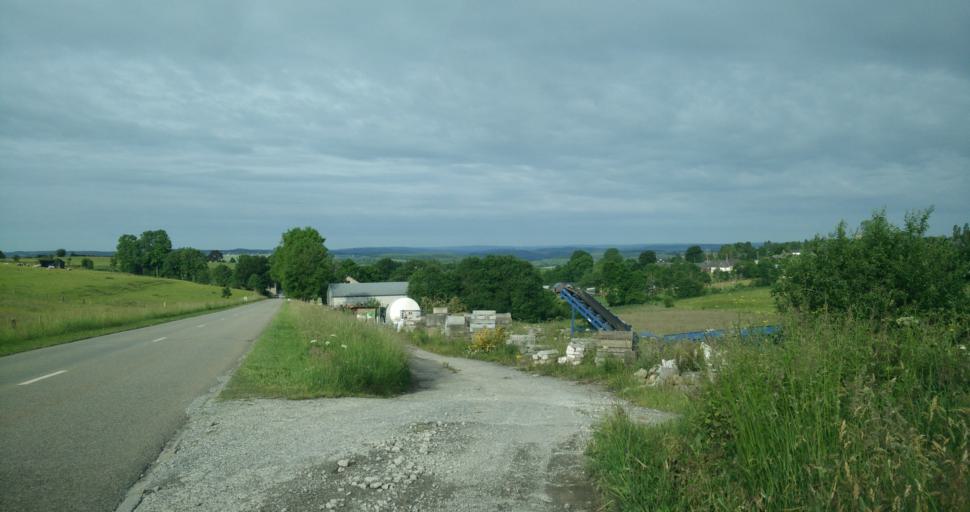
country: BE
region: Wallonia
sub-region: Province du Luxembourg
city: Houffalize
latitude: 50.1543
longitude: 5.7775
